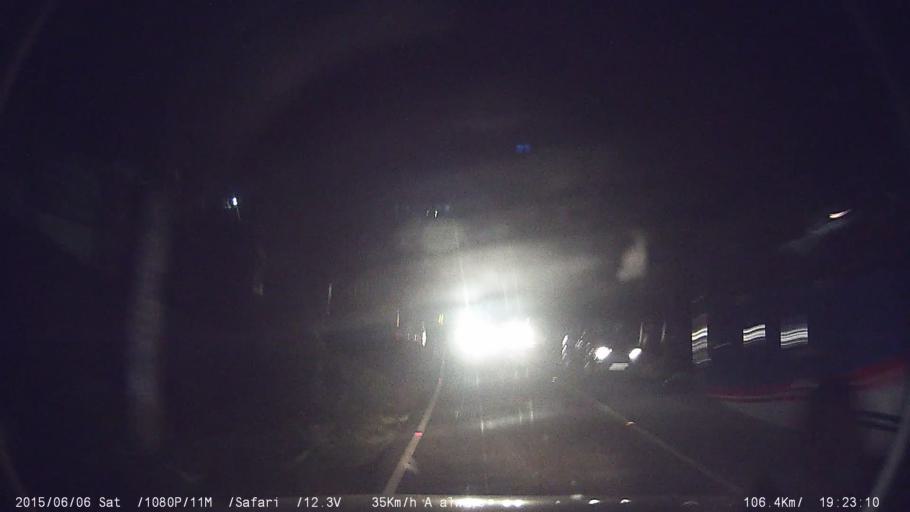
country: IN
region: Kerala
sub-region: Kottayam
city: Kottayam
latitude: 9.5724
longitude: 76.5798
